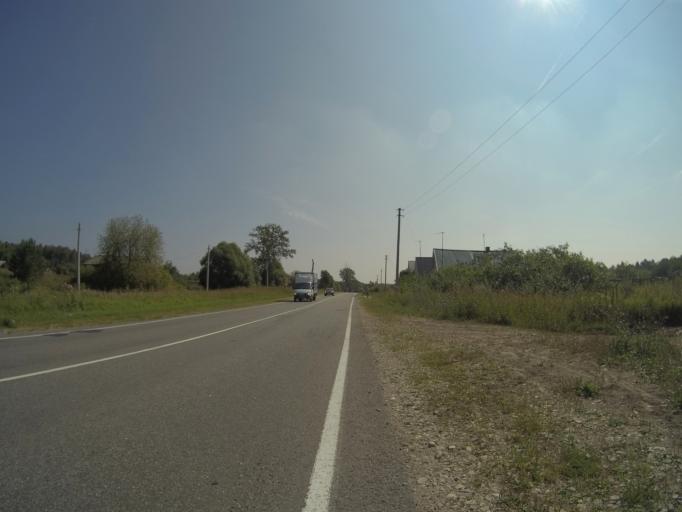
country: RU
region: Vladimir
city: Anopino
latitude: 55.7428
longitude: 40.6970
